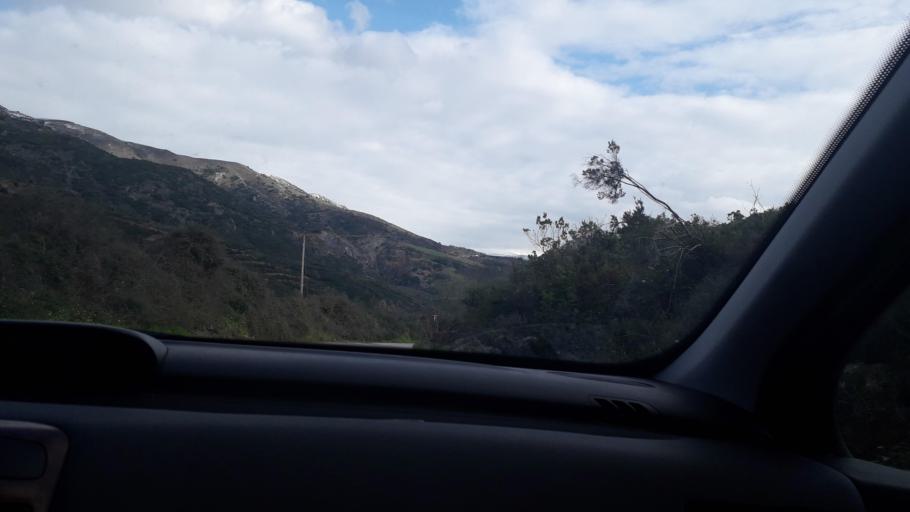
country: GR
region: Crete
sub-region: Nomos Rethymnis
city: Agia Foteini
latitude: 35.2969
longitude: 24.5517
